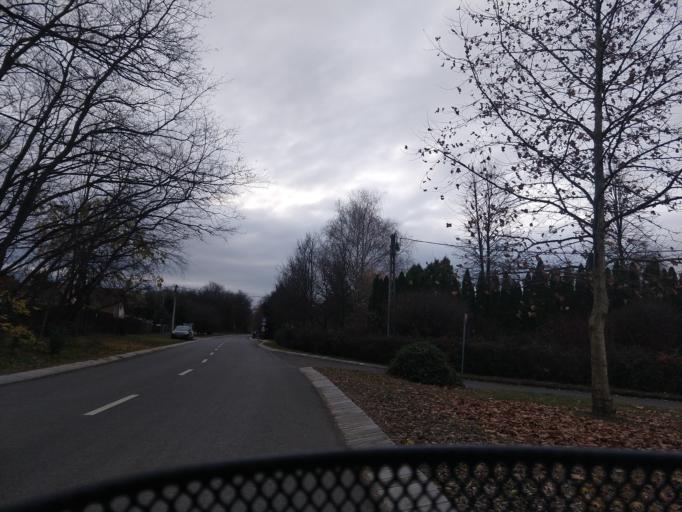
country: HU
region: Pest
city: Veresegyhaz
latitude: 47.6507
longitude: 19.2673
